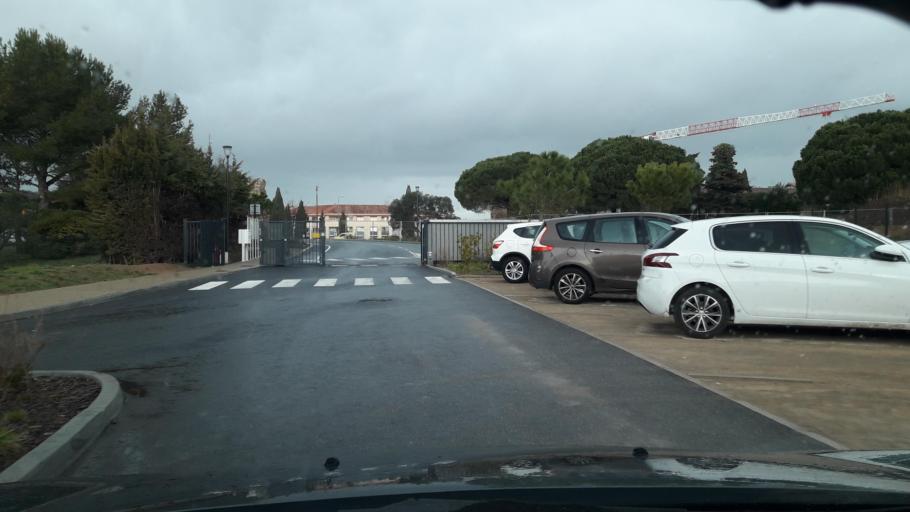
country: FR
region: Provence-Alpes-Cote d'Azur
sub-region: Departement du Var
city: Frejus
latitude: 43.4376
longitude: 6.7436
